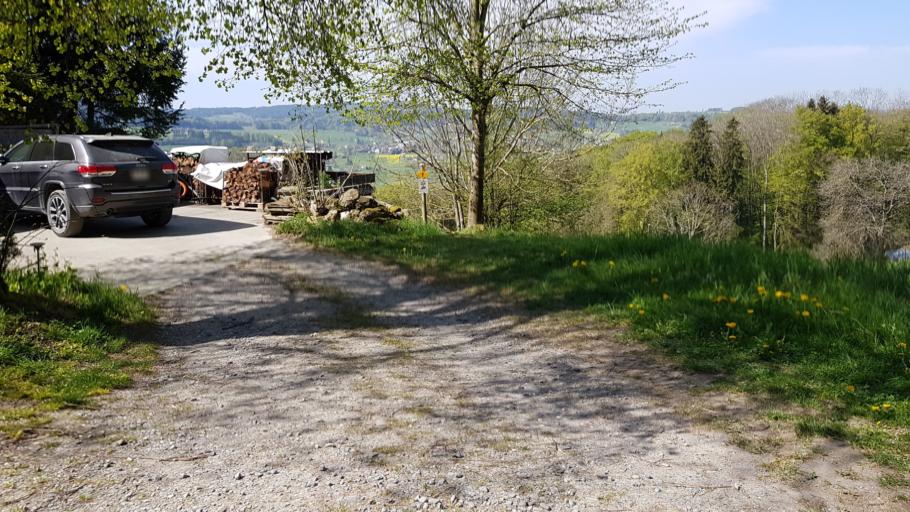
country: CH
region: Aargau
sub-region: Bezirk Kulm
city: Reinach
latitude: 47.2757
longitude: 8.1751
